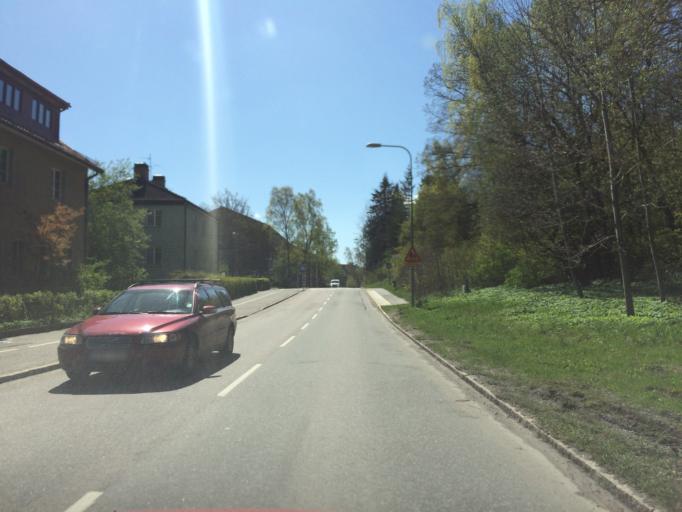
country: SE
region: Stockholm
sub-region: Huddinge Kommun
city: Segeltorp
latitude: 59.2991
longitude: 17.9567
